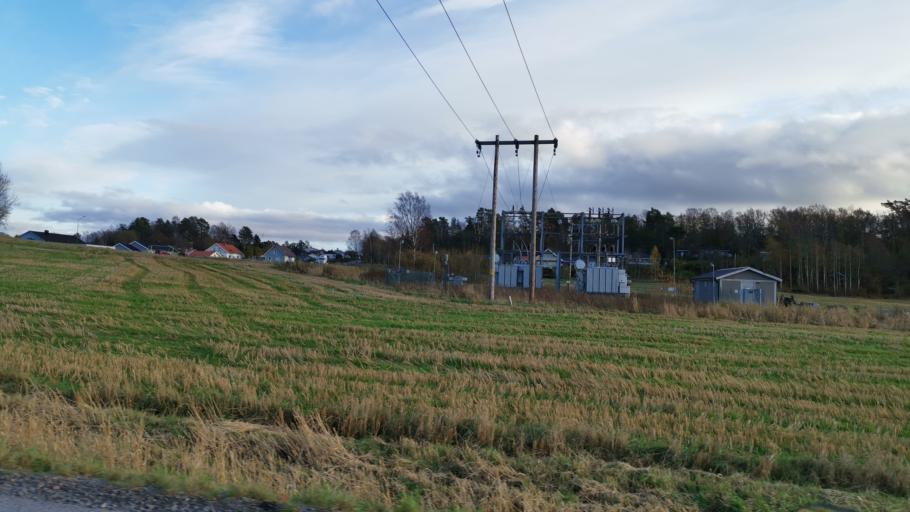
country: SE
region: Vaestra Goetaland
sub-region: Munkedals Kommun
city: Munkedal
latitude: 58.4657
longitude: 11.6594
